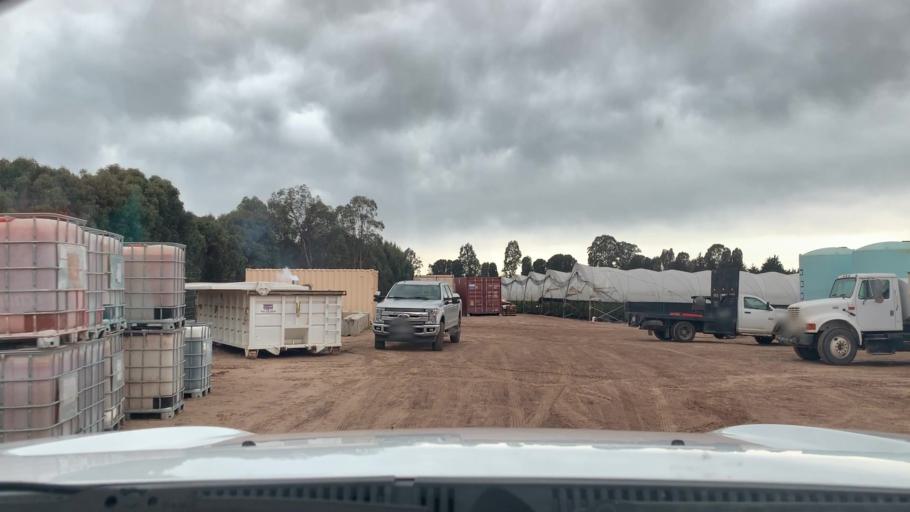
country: US
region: California
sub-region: San Luis Obispo County
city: Callender
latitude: 35.0622
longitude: -120.5671
